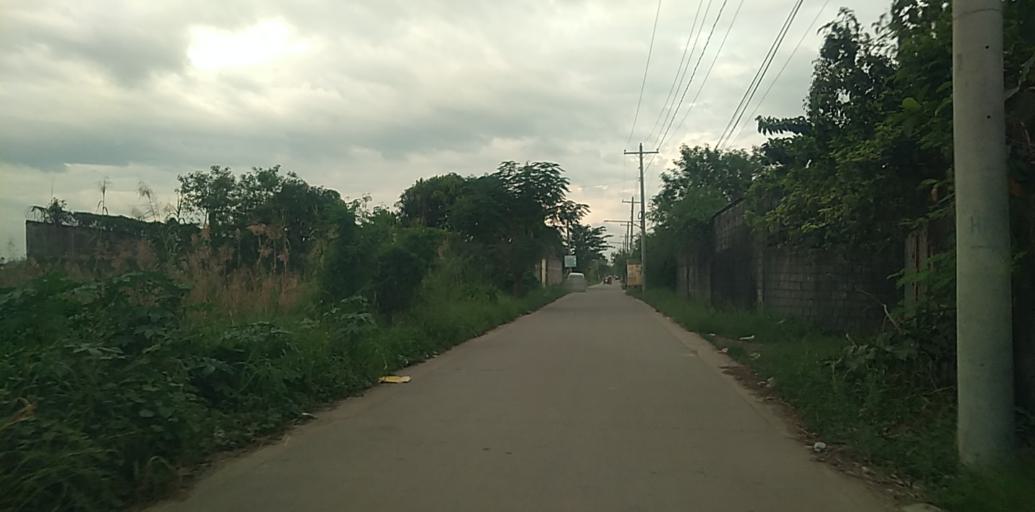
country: PH
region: Central Luzon
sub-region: Province of Pampanga
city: San Fernando
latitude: 15.0064
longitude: 120.7040
